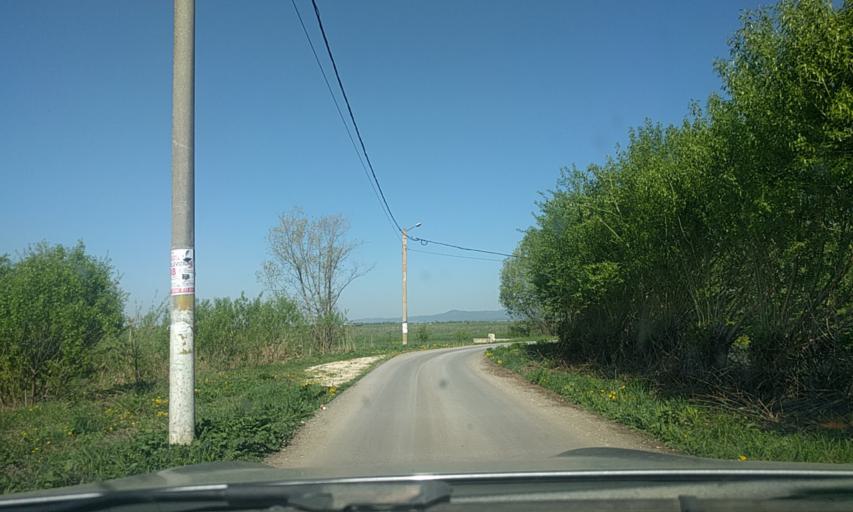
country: RO
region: Brasov
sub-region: Comuna Bod
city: Colonia Bod
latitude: 45.7196
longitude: 25.5665
